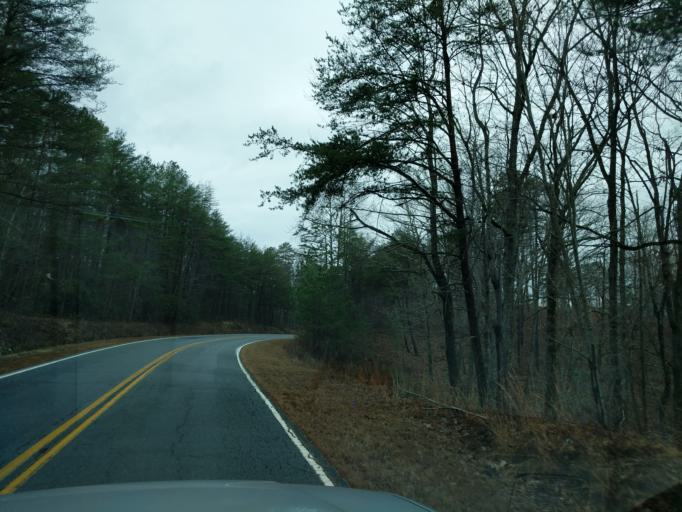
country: US
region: South Carolina
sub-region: Oconee County
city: Walhalla
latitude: 34.7879
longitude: -83.1916
